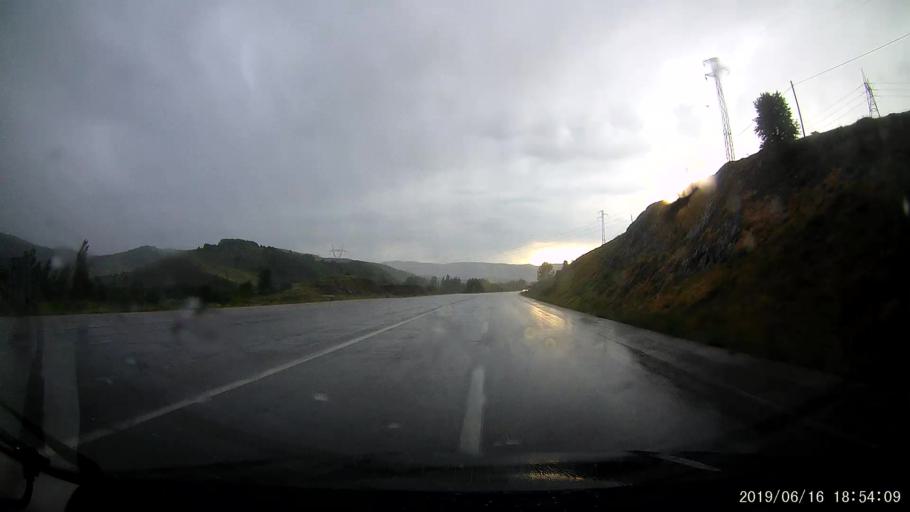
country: TR
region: Erzincan
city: Catalcam
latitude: 39.8964
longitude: 38.8602
